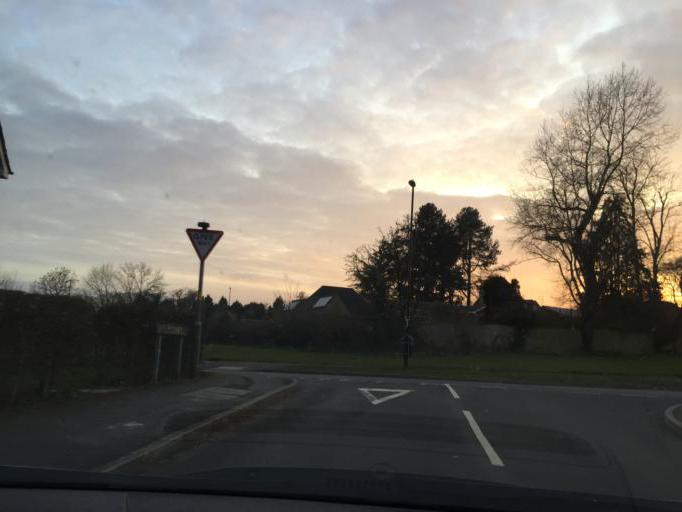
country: GB
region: England
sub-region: Warwickshire
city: Kenilworth
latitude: 52.3887
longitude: -1.5927
